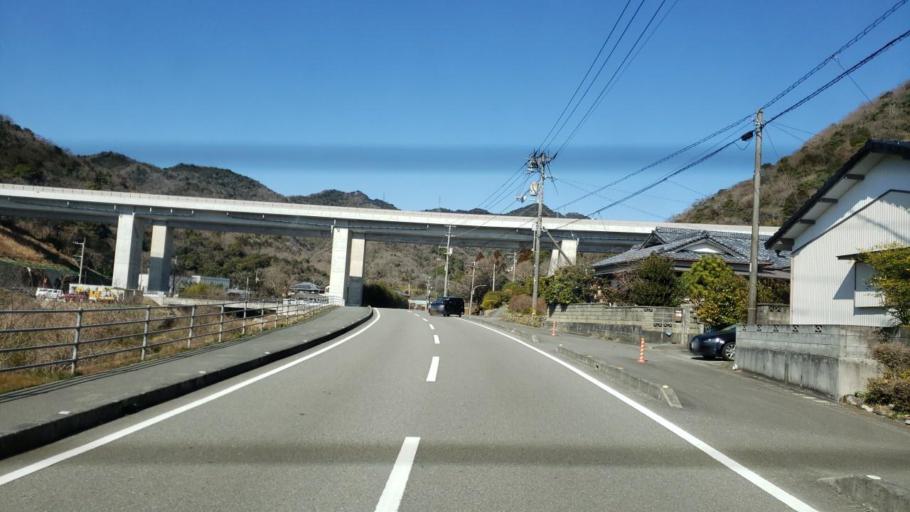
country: JP
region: Tokushima
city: Narutocho-mitsuishi
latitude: 34.1650
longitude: 134.5413
